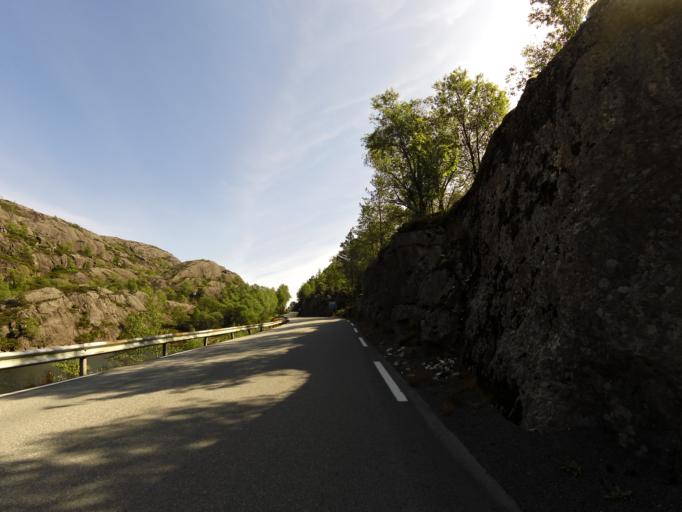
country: NO
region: Rogaland
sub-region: Sokndal
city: Hauge i Dalane
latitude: 58.3375
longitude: 6.3489
